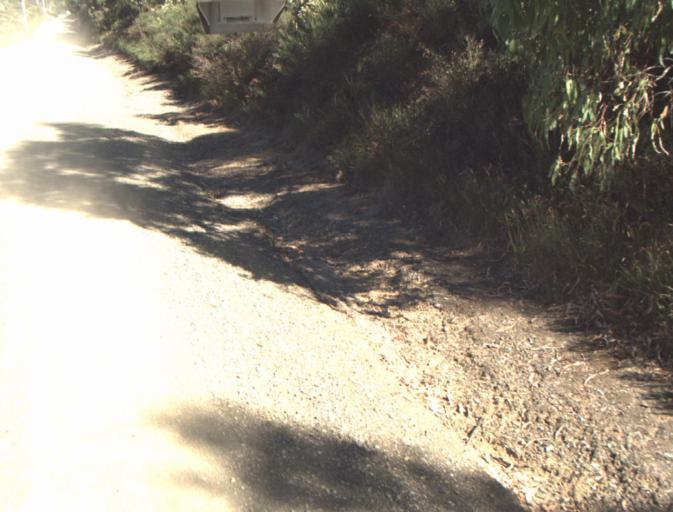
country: AU
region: Tasmania
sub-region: Launceston
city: Newstead
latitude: -41.3223
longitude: 147.3290
